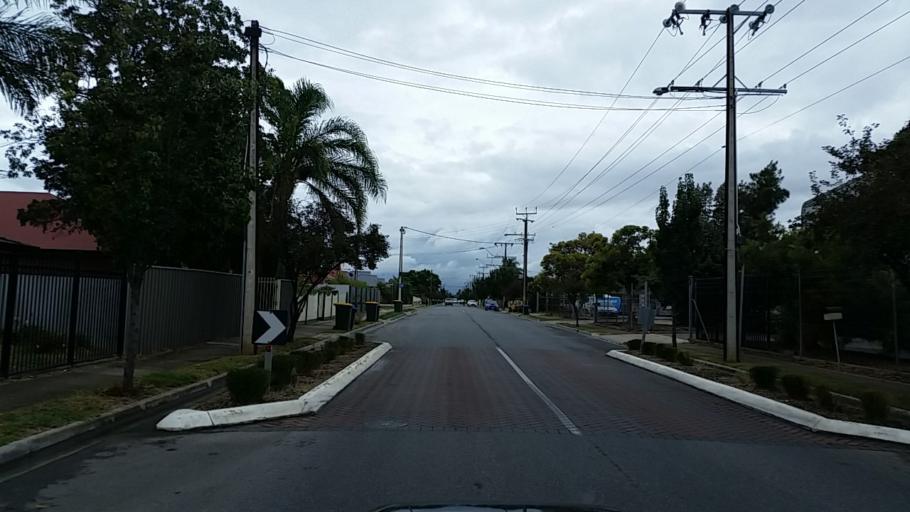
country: AU
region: South Australia
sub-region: Charles Sturt
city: Findon
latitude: -34.8954
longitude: 138.5414
